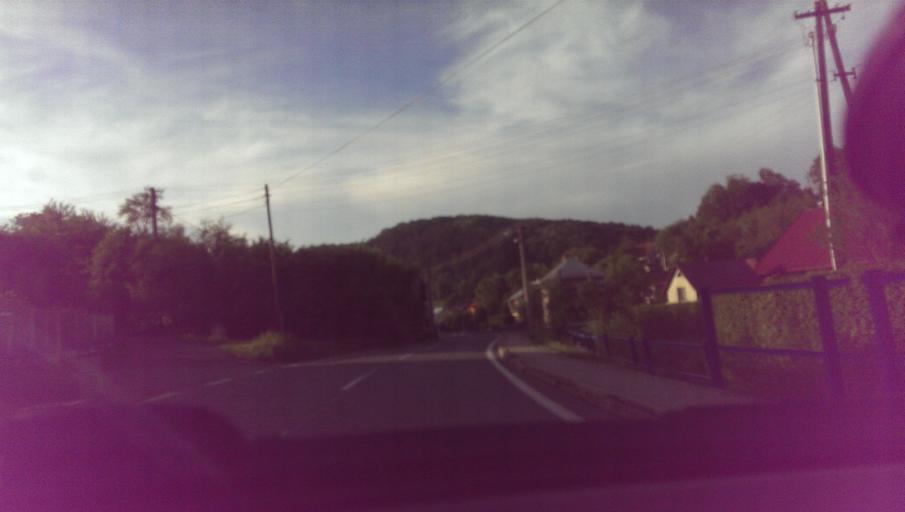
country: CZ
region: Zlin
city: Valasska Polanka
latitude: 49.2345
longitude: 17.9548
